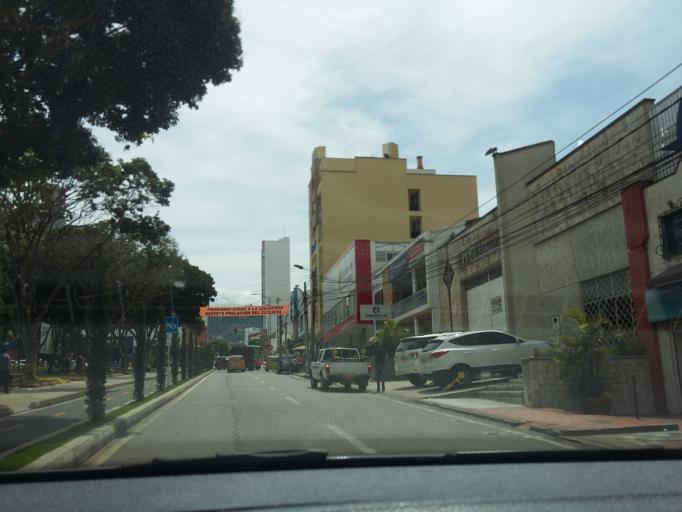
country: CO
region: Santander
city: Bucaramanga
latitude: 7.1243
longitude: -73.1188
